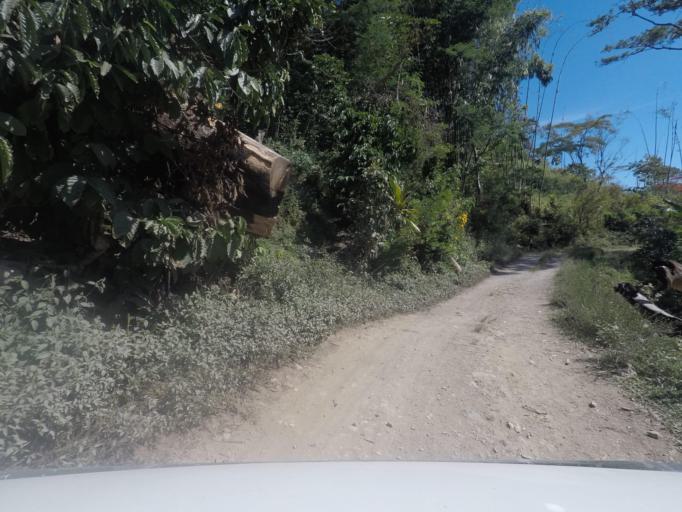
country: TL
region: Ermera
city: Gleno
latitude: -8.7246
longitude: 125.3323
